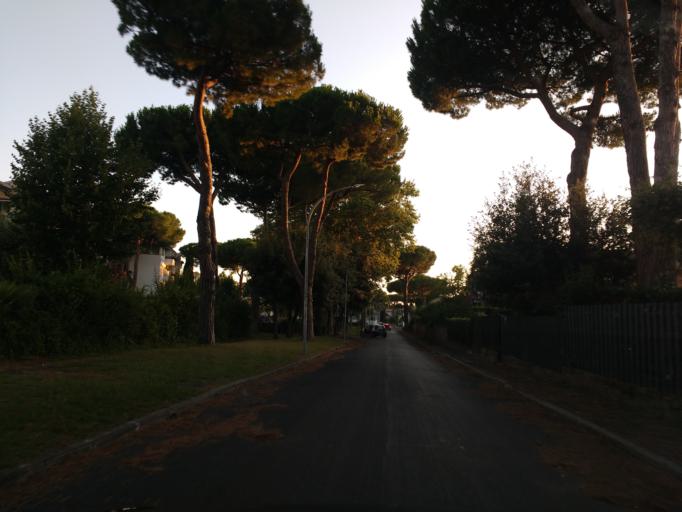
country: IT
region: Latium
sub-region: Citta metropolitana di Roma Capitale
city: Acilia-Castel Fusano-Ostia Antica
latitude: 41.7596
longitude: 12.3625
